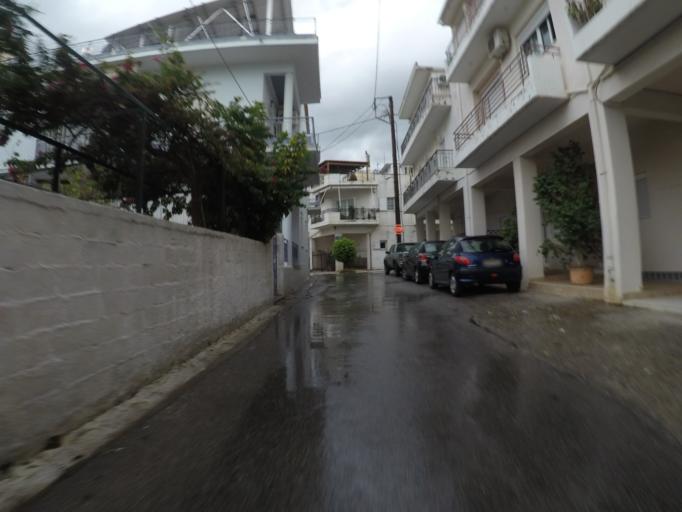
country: GR
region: Peloponnese
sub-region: Nomos Messinias
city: Kalamata
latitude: 37.0400
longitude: 22.1054
